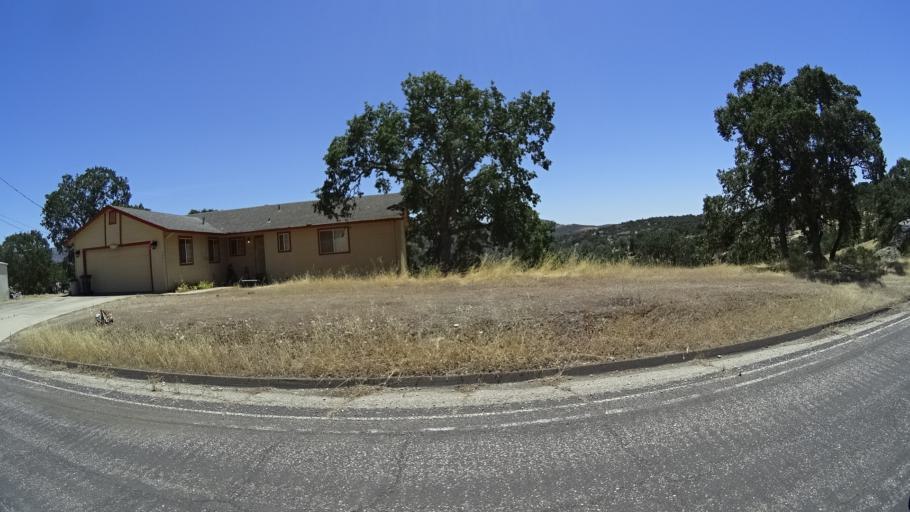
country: US
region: California
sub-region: Calaveras County
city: Rancho Calaveras
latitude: 38.1518
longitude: -120.8397
